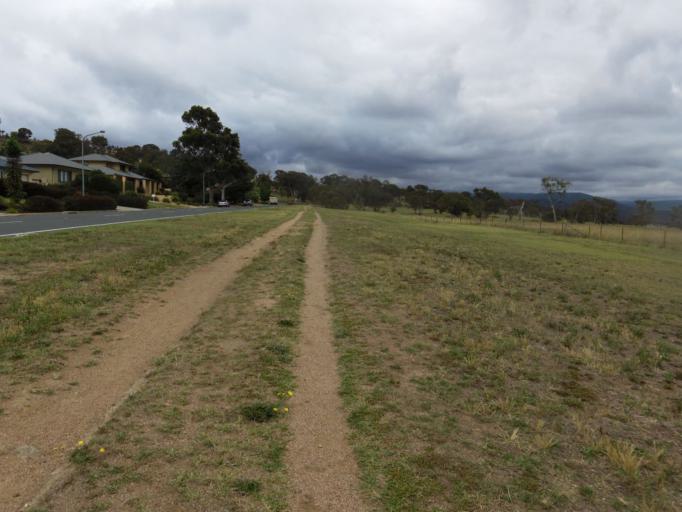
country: AU
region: Australian Capital Territory
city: Macquarie
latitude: -35.3481
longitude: 149.0260
